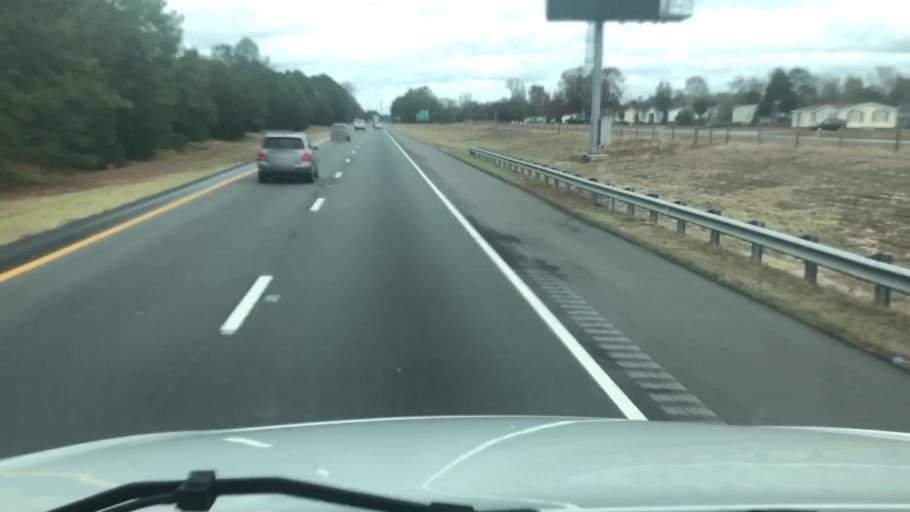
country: US
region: North Carolina
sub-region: Cumberland County
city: Vander
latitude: 35.0630
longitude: -78.7936
